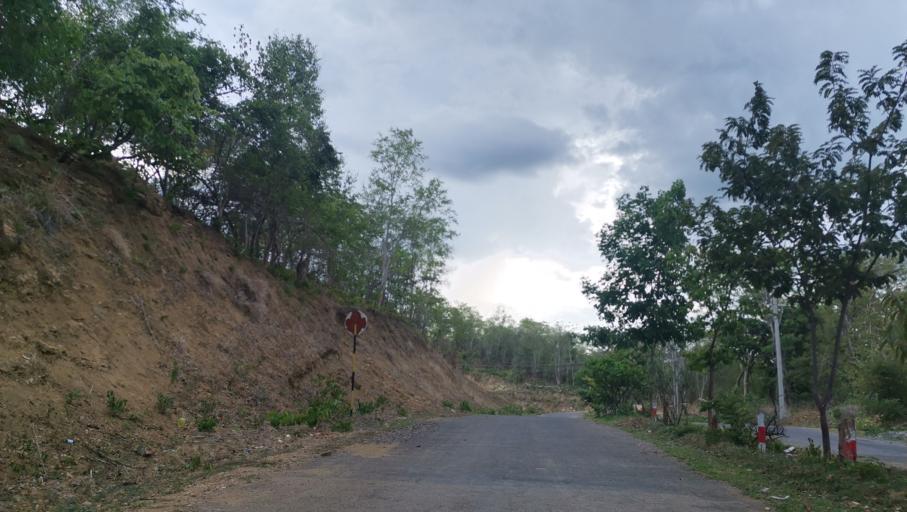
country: MM
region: Magway
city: Minbu
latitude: 20.1048
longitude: 94.5471
